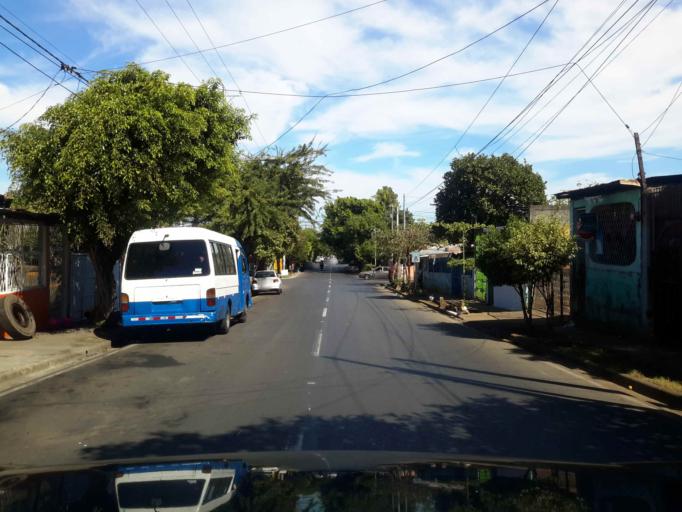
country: NI
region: Managua
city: Managua
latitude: 12.1129
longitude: -86.2970
